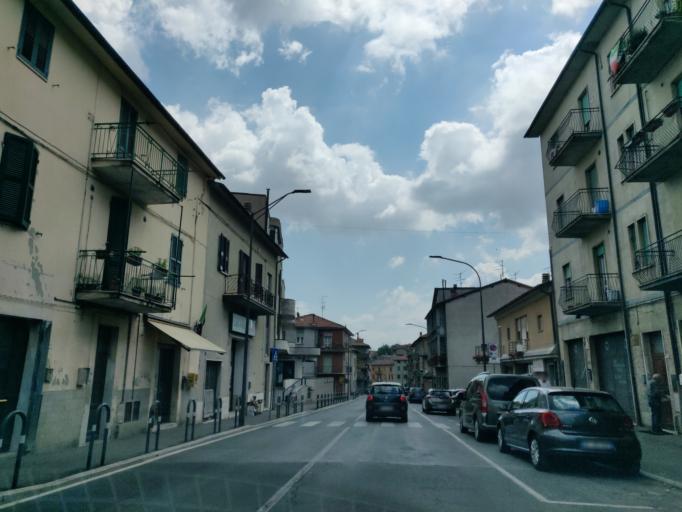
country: IT
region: Tuscany
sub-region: Provincia di Siena
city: Abbadia San Salvatore
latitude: 42.8793
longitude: 11.6758
